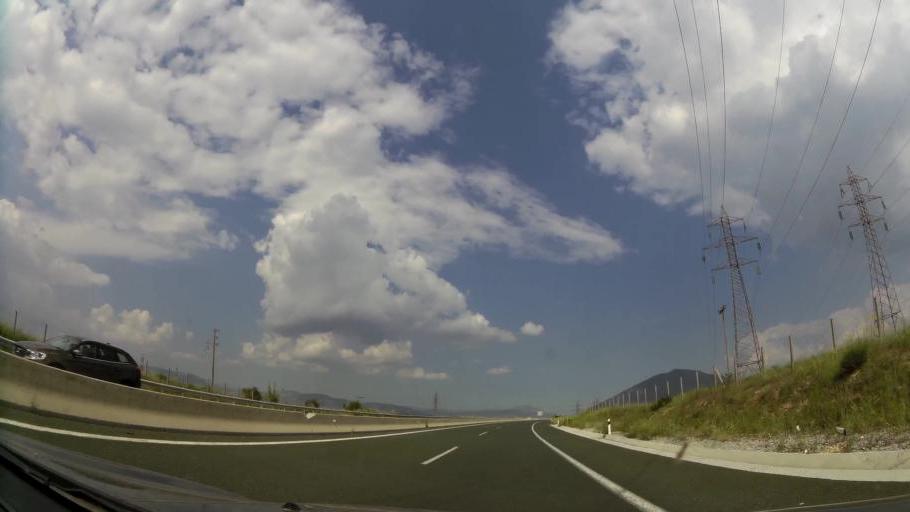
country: GR
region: West Macedonia
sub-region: Nomos Kozanis
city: Koila
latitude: 40.3622
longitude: 21.8231
